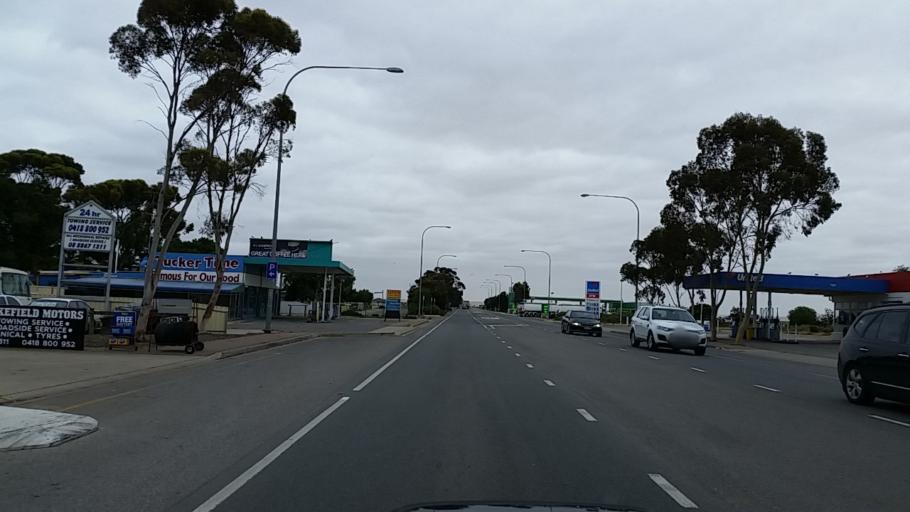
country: AU
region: South Australia
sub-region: Wakefield
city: Balaklava
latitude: -34.1829
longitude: 138.1536
